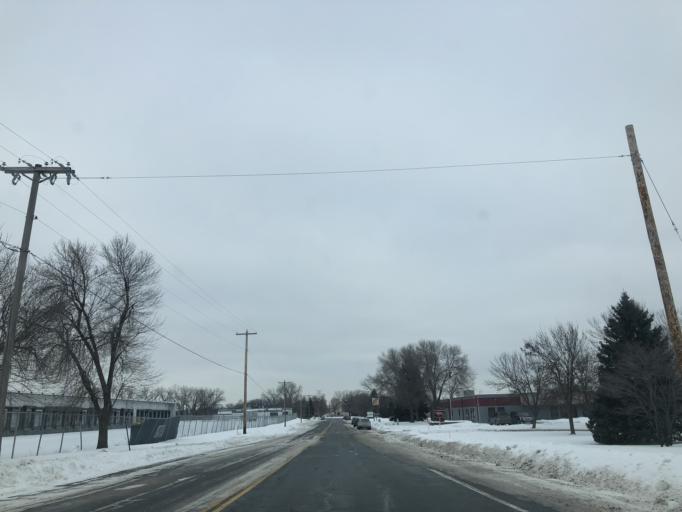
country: US
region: Minnesota
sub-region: Ramsey County
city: New Brighton
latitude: 45.0719
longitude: -93.1882
